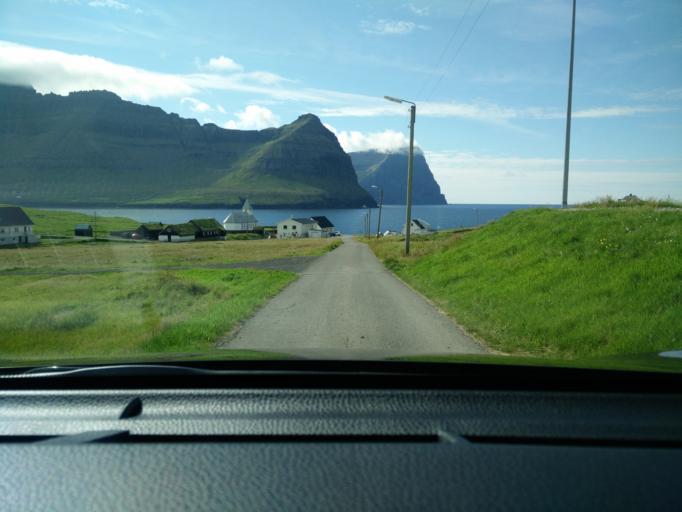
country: FO
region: Nordoyar
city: Klaksvik
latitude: 62.3604
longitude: -6.5389
